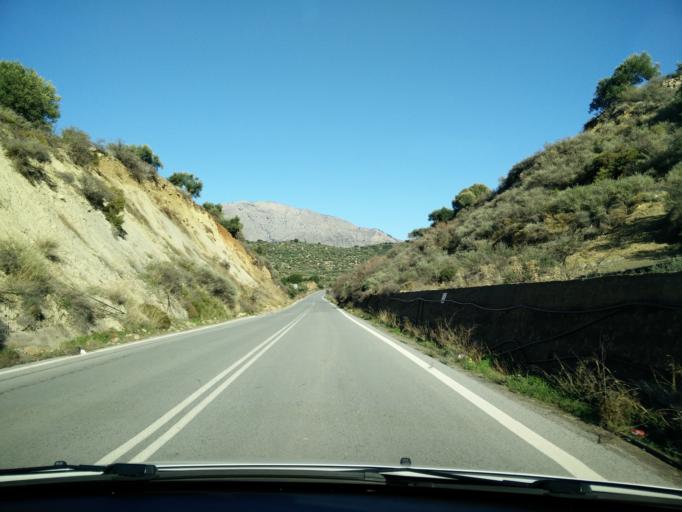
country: GR
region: Crete
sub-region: Nomos Irakleiou
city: Arkalochori
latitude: 35.0761
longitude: 25.3476
